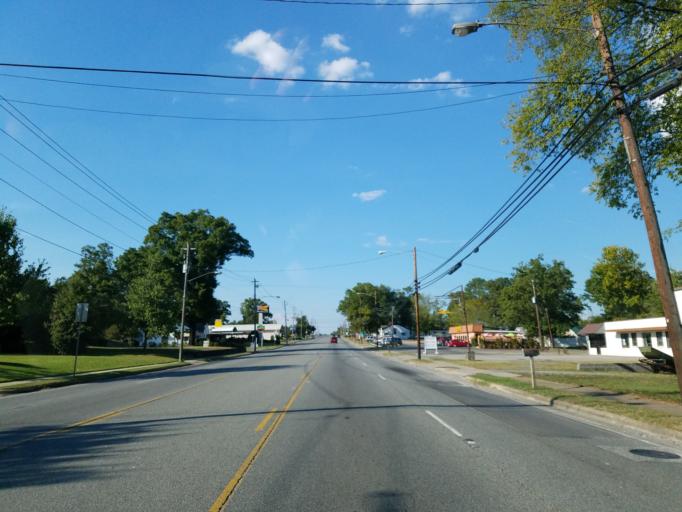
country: US
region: Georgia
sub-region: Murray County
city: Chatsworth
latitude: 34.7717
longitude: -84.7696
